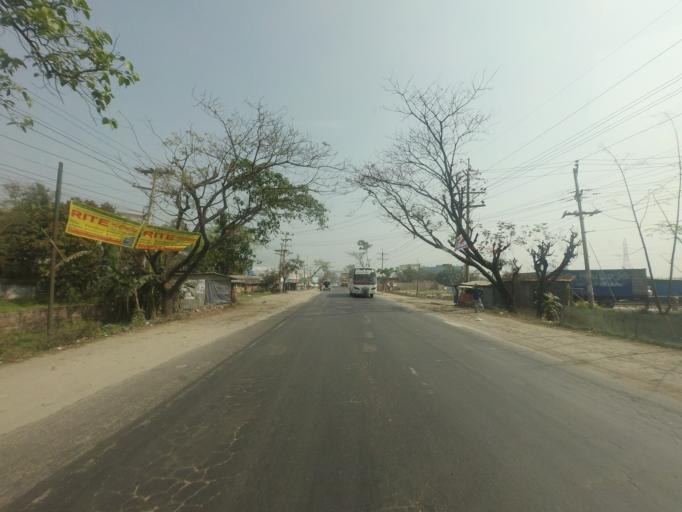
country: BD
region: Dhaka
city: Narsingdi
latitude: 23.9149
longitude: 90.6910
